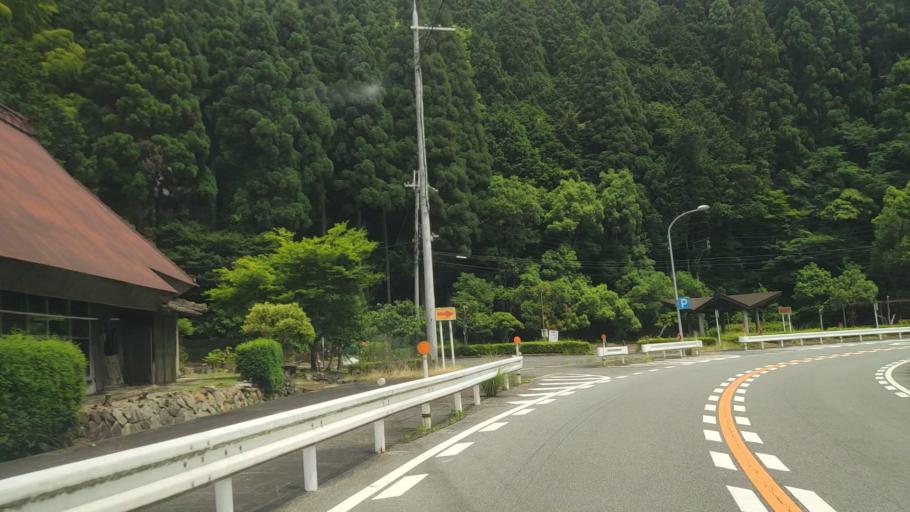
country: JP
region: Hyogo
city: Yamazakicho-nakabirose
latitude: 35.0712
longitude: 134.3606
